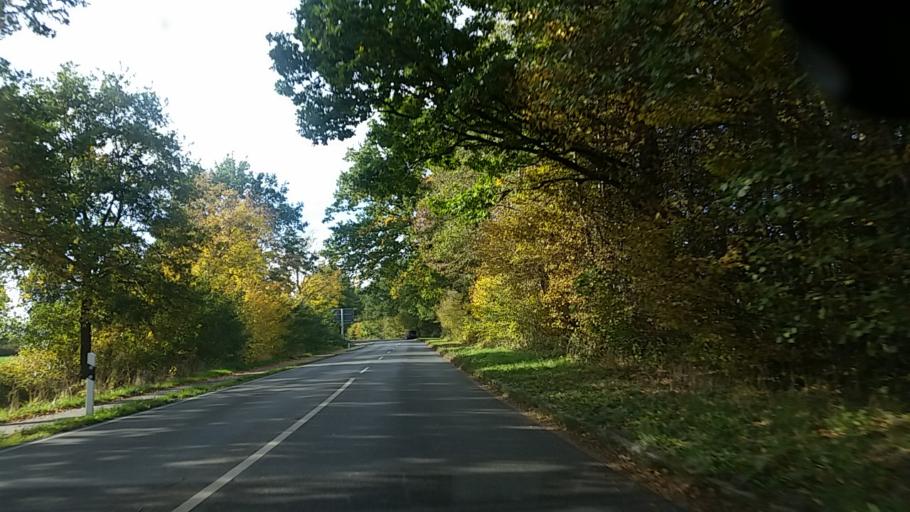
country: DE
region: Schleswig-Holstein
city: Bargteheide
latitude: 53.7348
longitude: 10.2460
